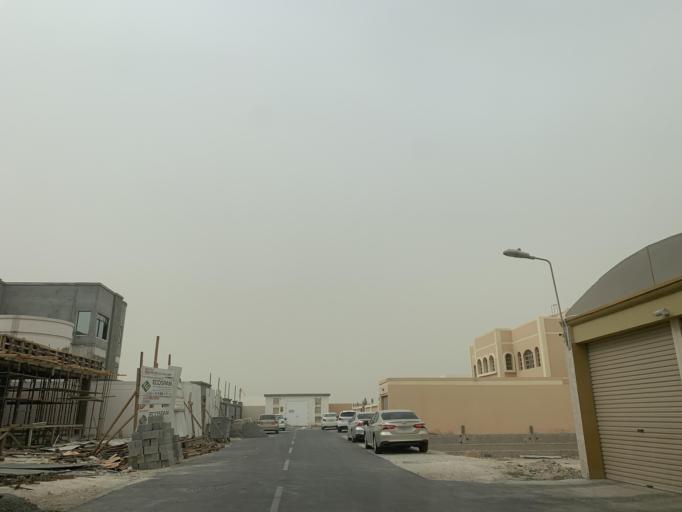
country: BH
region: Northern
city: Ar Rifa'
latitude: 26.1445
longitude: 50.5375
